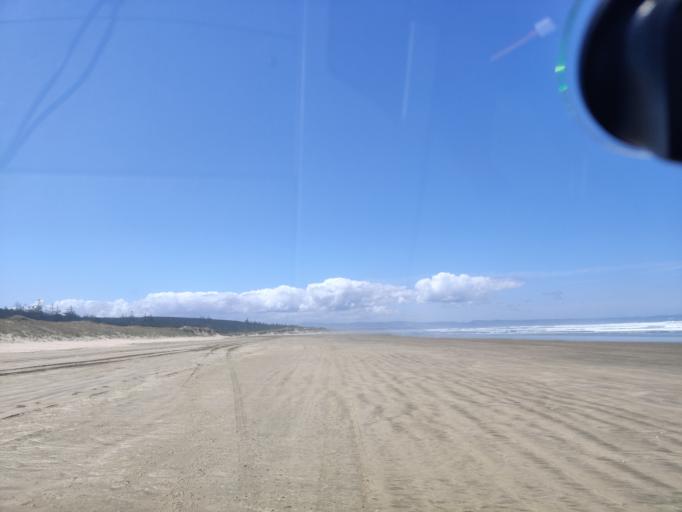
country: NZ
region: Northland
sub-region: Far North District
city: Kaitaia
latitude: -35.0002
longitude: 173.1514
